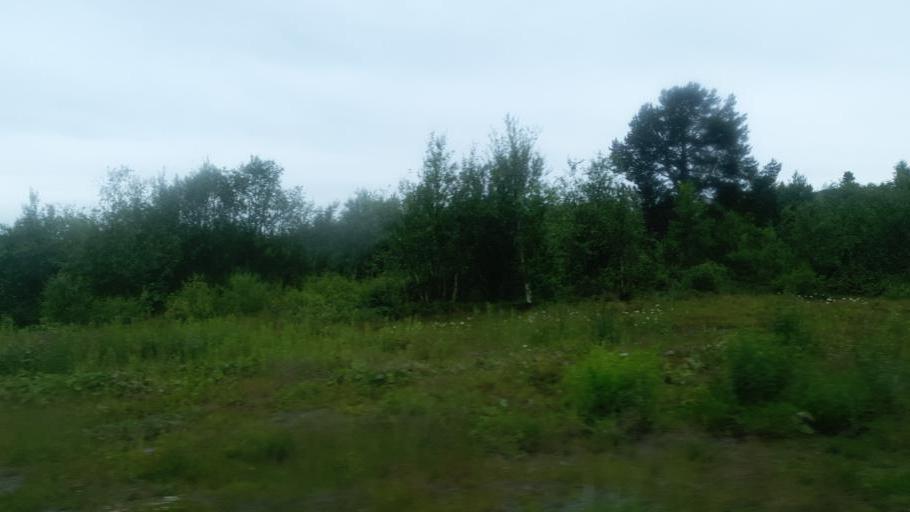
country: NO
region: Oppland
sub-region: Vestre Slidre
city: Slidre
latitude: 61.2383
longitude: 8.9155
